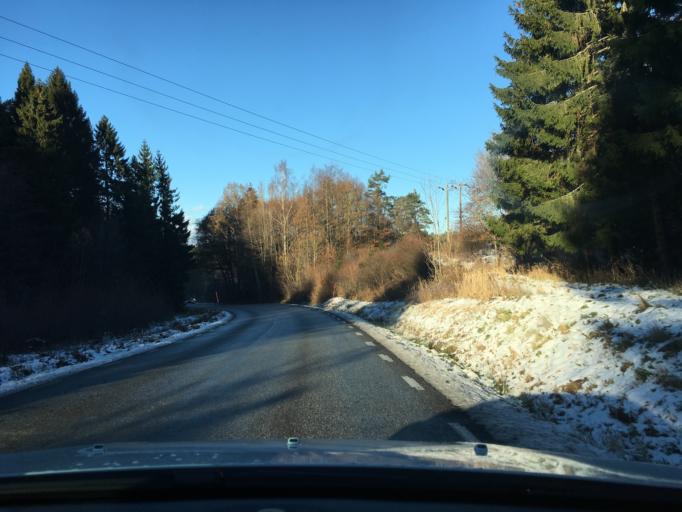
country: SE
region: Vaestra Goetaland
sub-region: Tjorns Kommun
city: Myggenas
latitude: 58.0486
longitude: 11.6743
